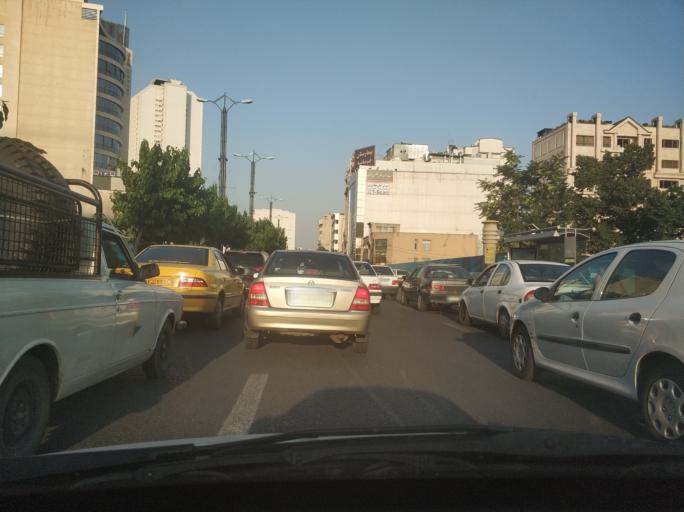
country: IR
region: Tehran
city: Tajrish
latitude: 35.7993
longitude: 51.4715
